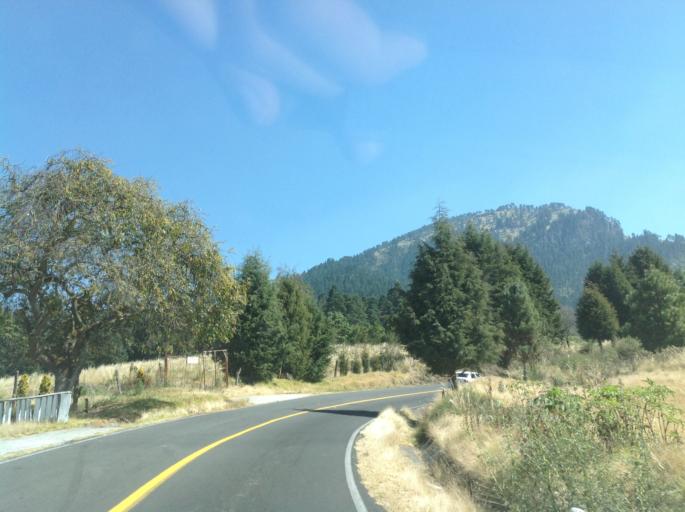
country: MX
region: Mexico
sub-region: Amecameca
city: San Diego Huehuecalco
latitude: 19.0749
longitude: -98.7010
